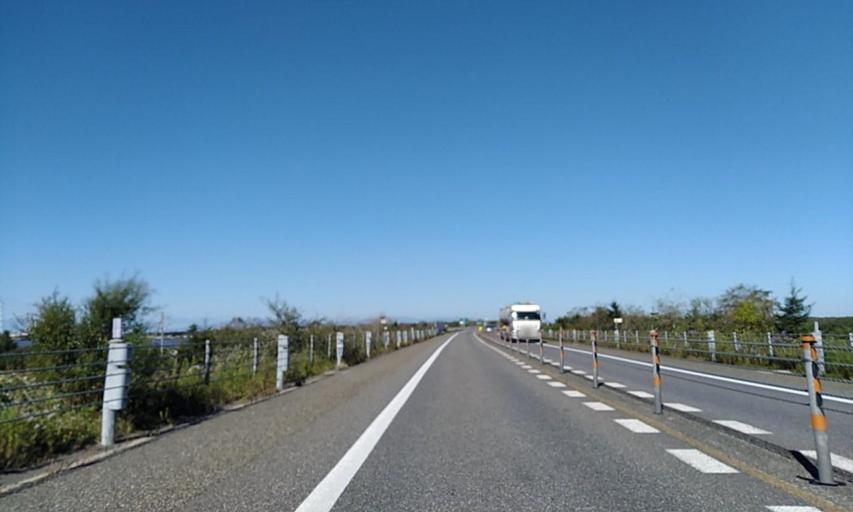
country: JP
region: Hokkaido
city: Tomakomai
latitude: 42.6131
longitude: 141.8513
